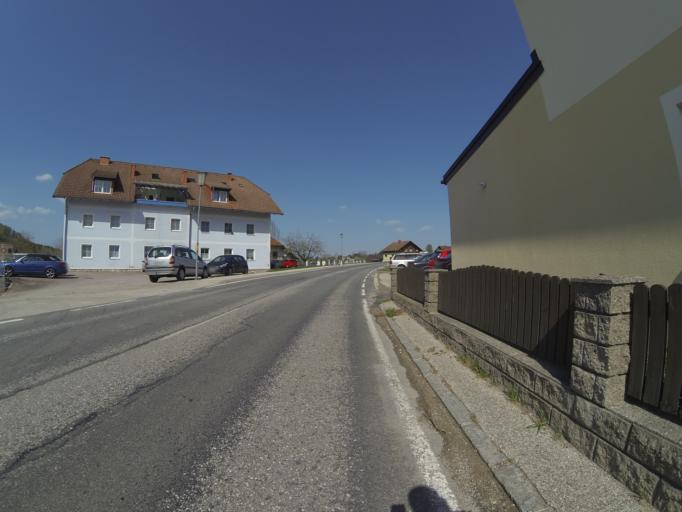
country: AT
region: Upper Austria
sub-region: Politischer Bezirk Gmunden
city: Altmunster
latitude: 47.9307
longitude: 13.7551
